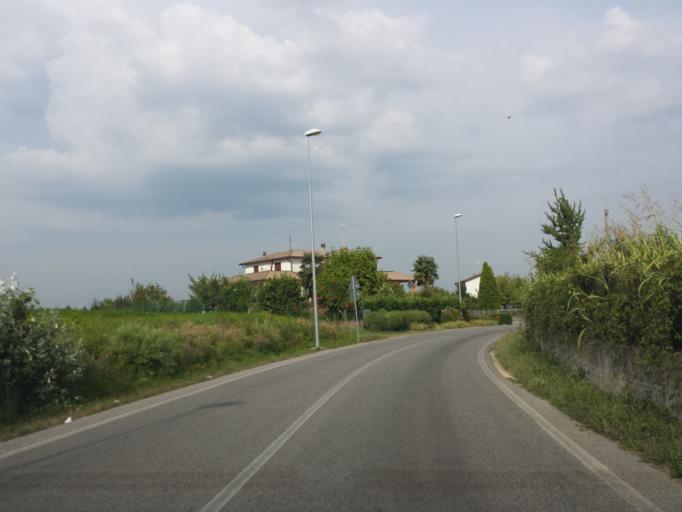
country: IT
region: Veneto
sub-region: Provincia di Vicenza
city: Creazzo
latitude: 45.5374
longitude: 11.4889
